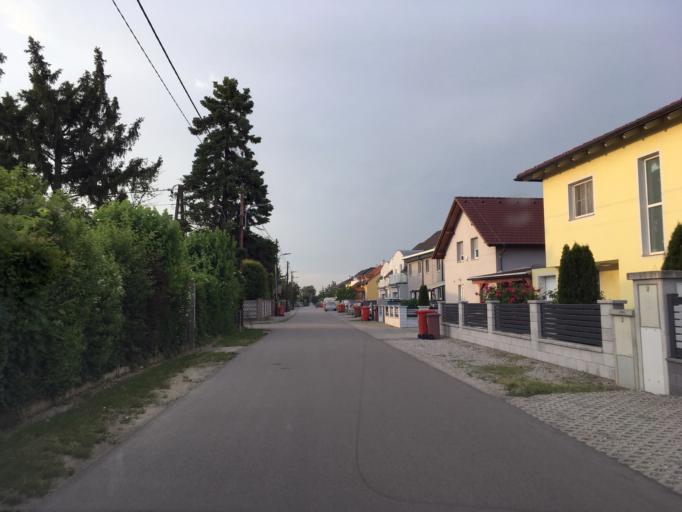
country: AT
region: Lower Austria
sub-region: Politischer Bezirk Wien-Umgebung
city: Gerasdorf bei Wien
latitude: 48.3157
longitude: 16.5027
